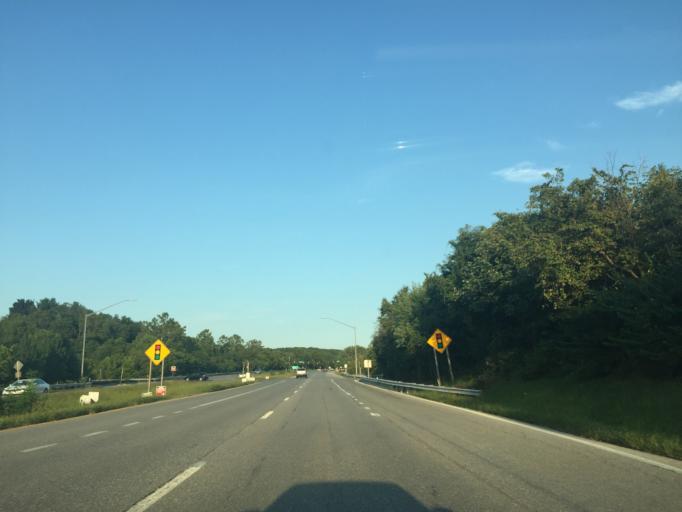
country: US
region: Maryland
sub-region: Frederick County
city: Spring Ridge
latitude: 39.3968
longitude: -77.3547
